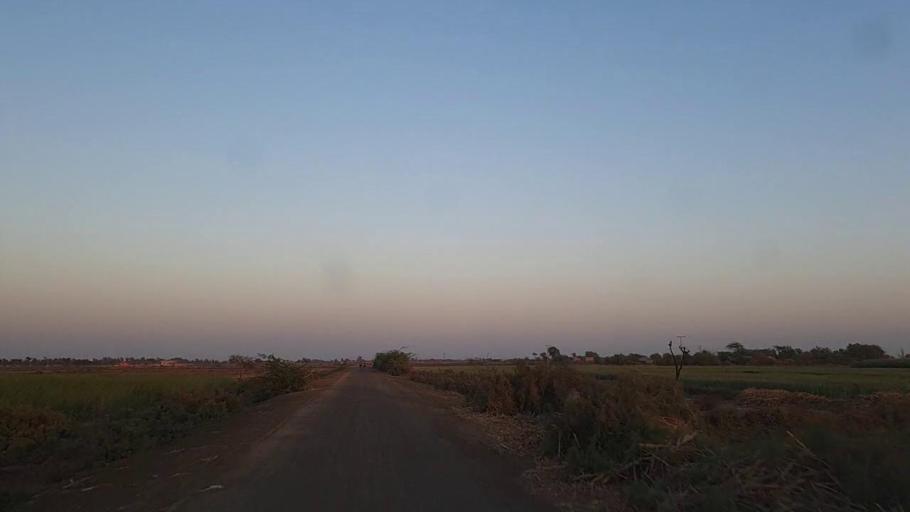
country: PK
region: Sindh
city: Samaro
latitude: 25.3094
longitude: 69.3824
